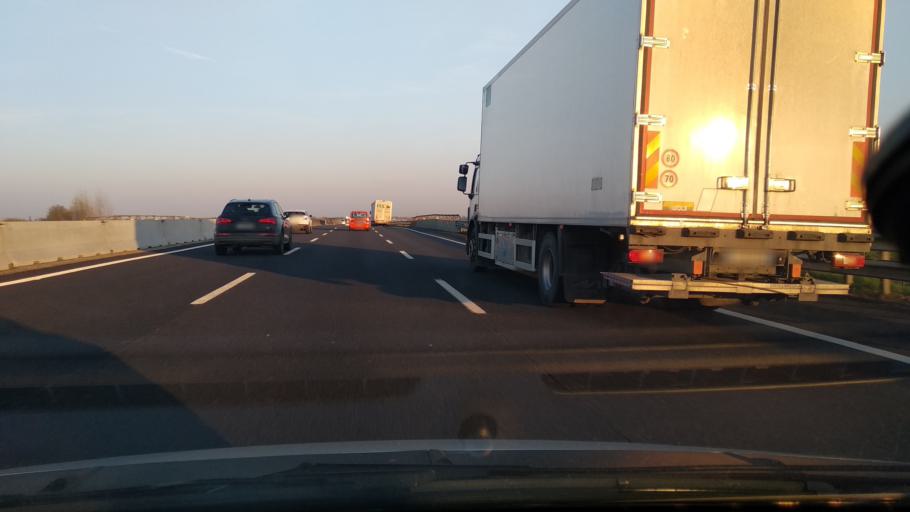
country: IT
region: Emilia-Romagna
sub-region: Provincia di Ravenna
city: Solarolo
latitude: 44.3507
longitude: 11.8256
